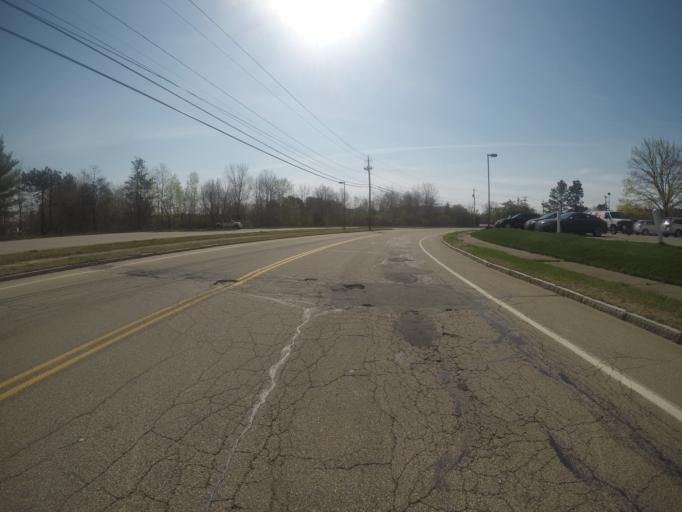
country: US
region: Massachusetts
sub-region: Bristol County
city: Easton
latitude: 42.0490
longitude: -71.0743
